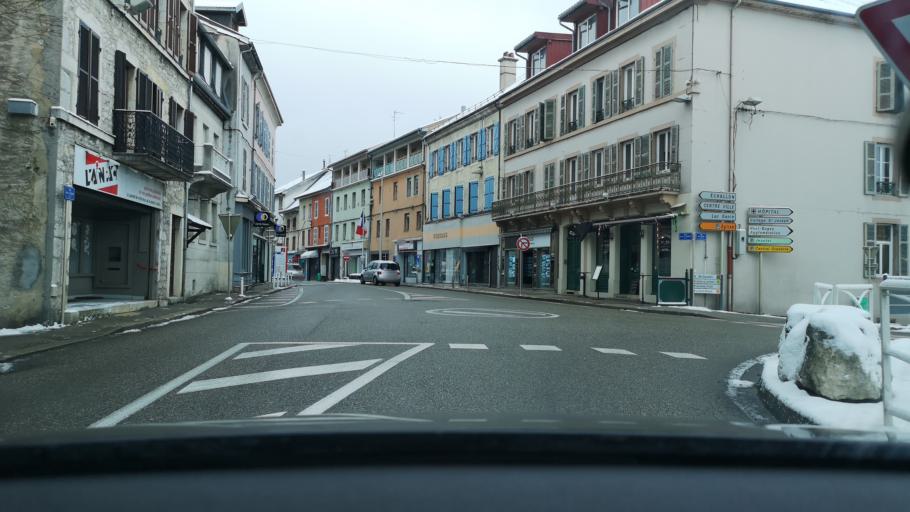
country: FR
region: Rhone-Alpes
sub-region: Departement de l'Ain
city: Oyonnax
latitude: 46.2604
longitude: 5.6583
